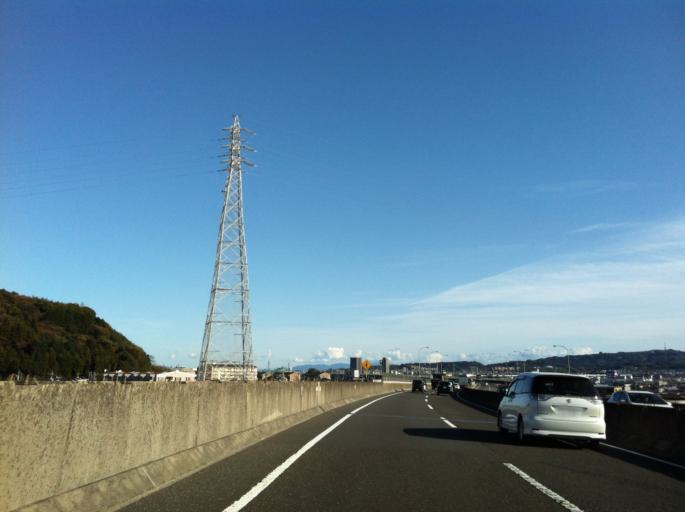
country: JP
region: Shizuoka
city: Shizuoka-shi
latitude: 35.0087
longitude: 138.4026
